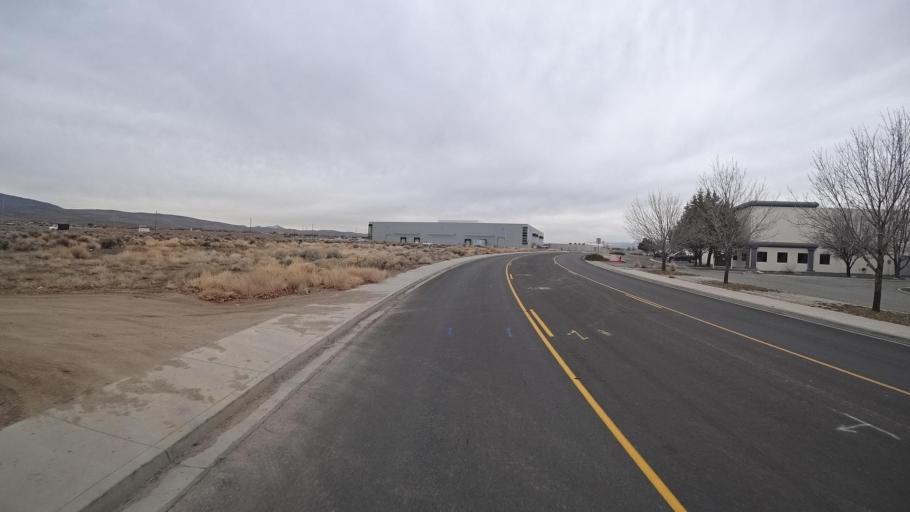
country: US
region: Nevada
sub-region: Washoe County
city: Spanish Springs
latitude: 39.6709
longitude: -119.7042
